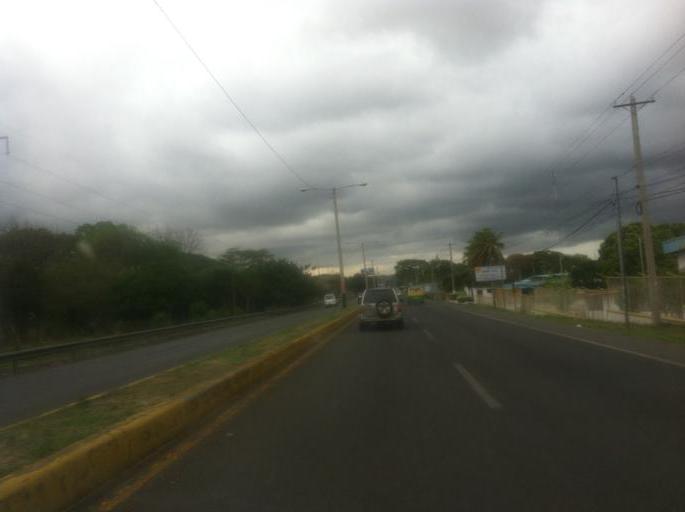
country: NI
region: Masaya
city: Ticuantepe
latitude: 12.0410
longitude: -86.1896
